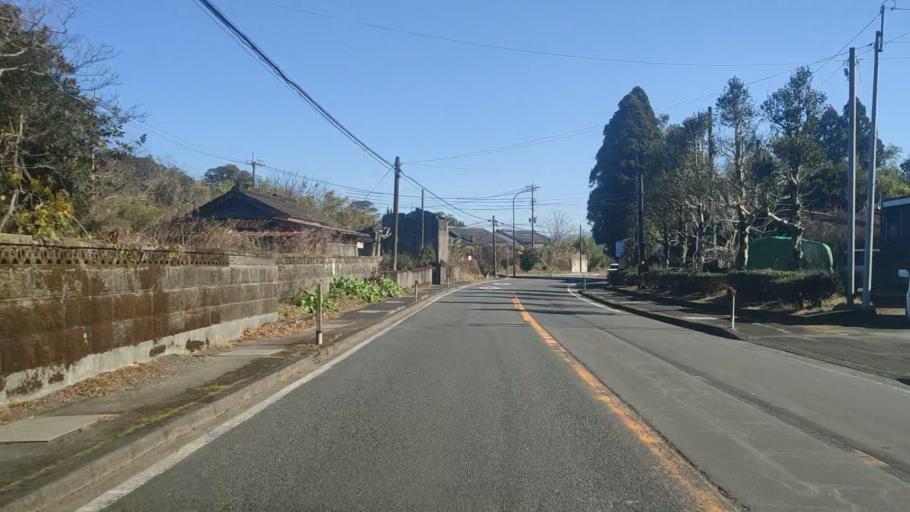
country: JP
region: Kagoshima
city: Sueyoshicho-ninokata
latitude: 31.6957
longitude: 130.9914
